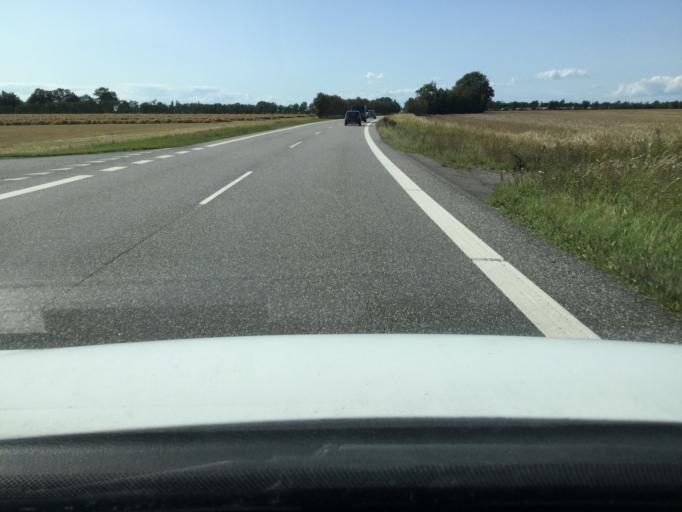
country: DK
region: Zealand
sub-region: Lolland Kommune
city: Nakskov
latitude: 54.8027
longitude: 11.2499
